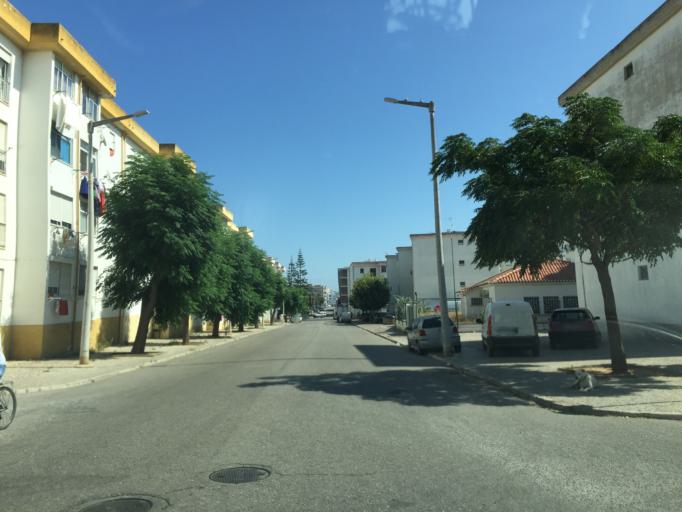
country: PT
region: Faro
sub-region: Olhao
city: Olhao
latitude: 37.0343
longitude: -7.8450
